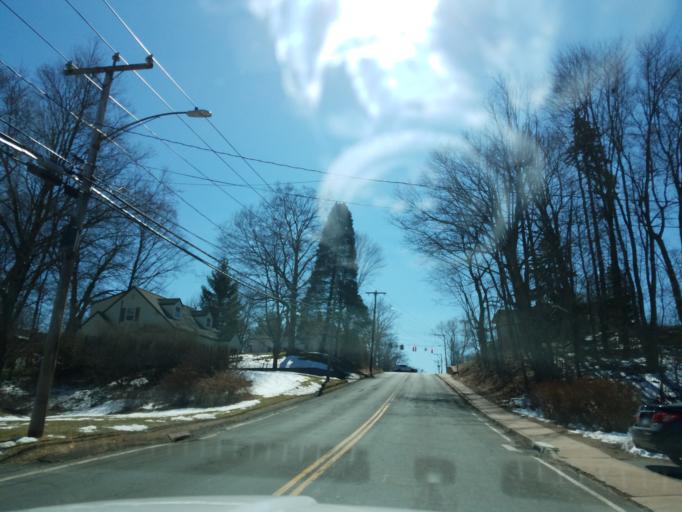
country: US
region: Connecticut
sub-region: Hartford County
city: Windsor Locks
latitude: 41.9269
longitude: -72.6332
